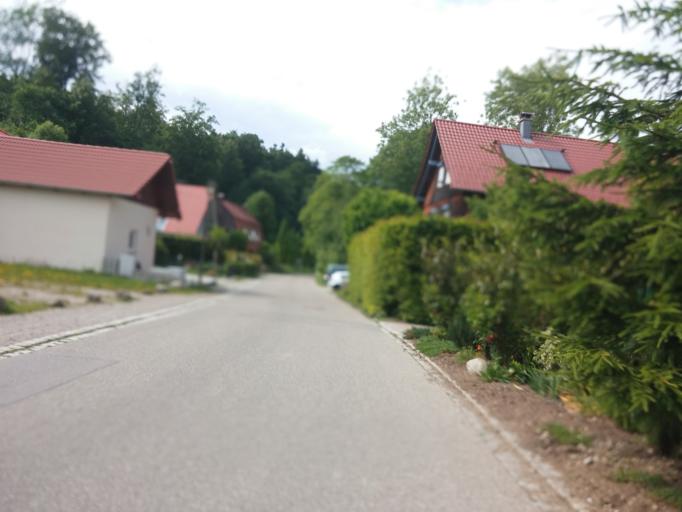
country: DE
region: Bavaria
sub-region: Swabia
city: Lautrach
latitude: 47.8997
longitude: 10.1147
